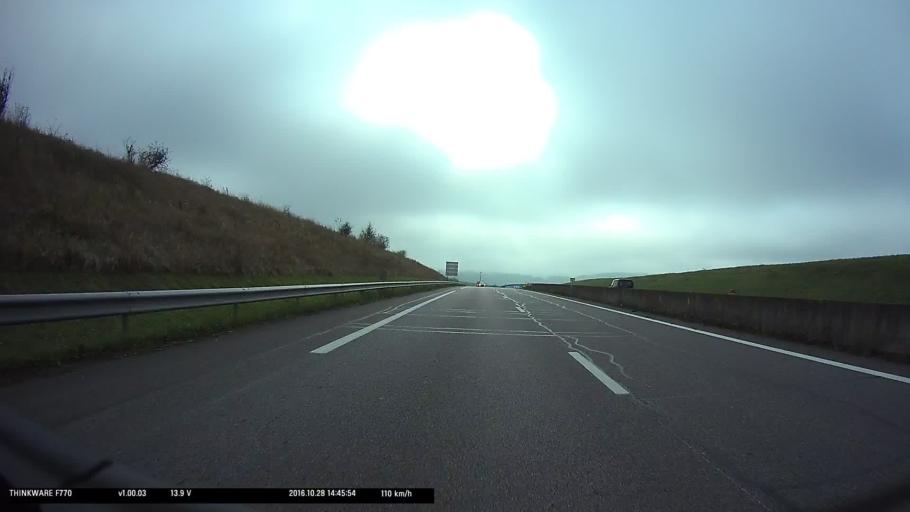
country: FR
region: Lorraine
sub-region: Departement de la Moselle
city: Sarrebourg
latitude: 48.7102
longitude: 7.0374
